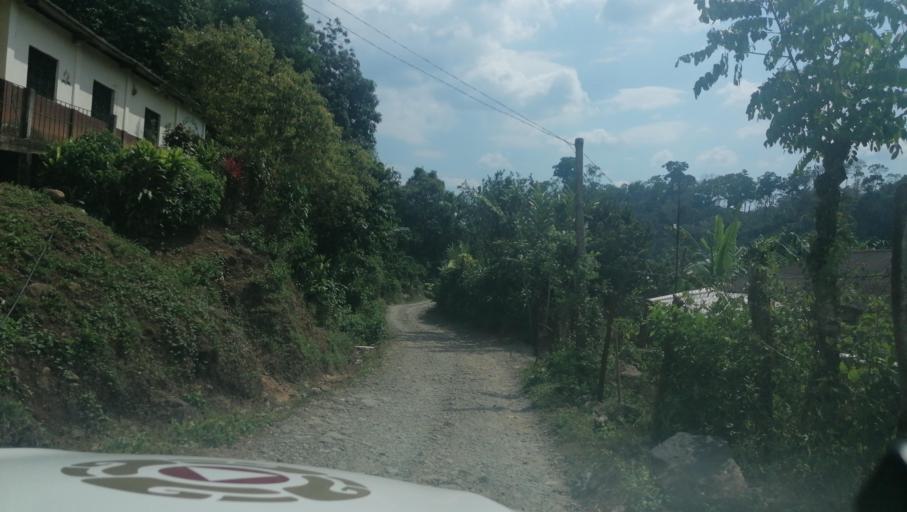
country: MX
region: Chiapas
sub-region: Cacahoatan
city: Benito Juarez
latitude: 15.0379
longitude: -92.2360
